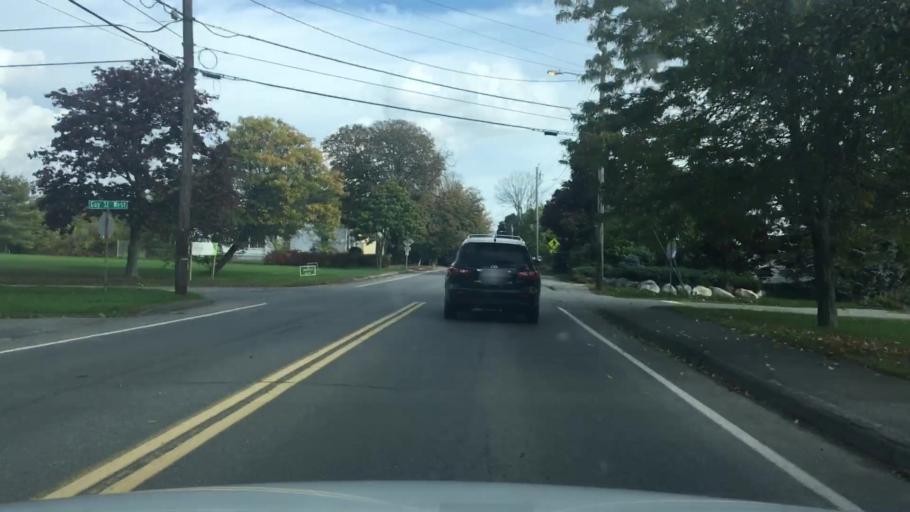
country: US
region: Maine
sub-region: Knox County
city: Rockland
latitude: 44.1116
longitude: -69.1153
